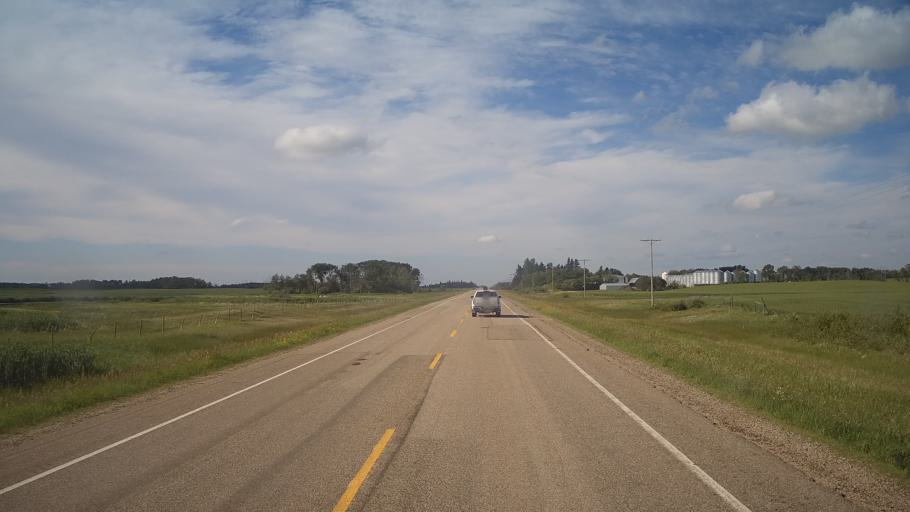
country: CA
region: Saskatchewan
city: Foam Lake
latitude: 51.5857
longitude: -103.8458
